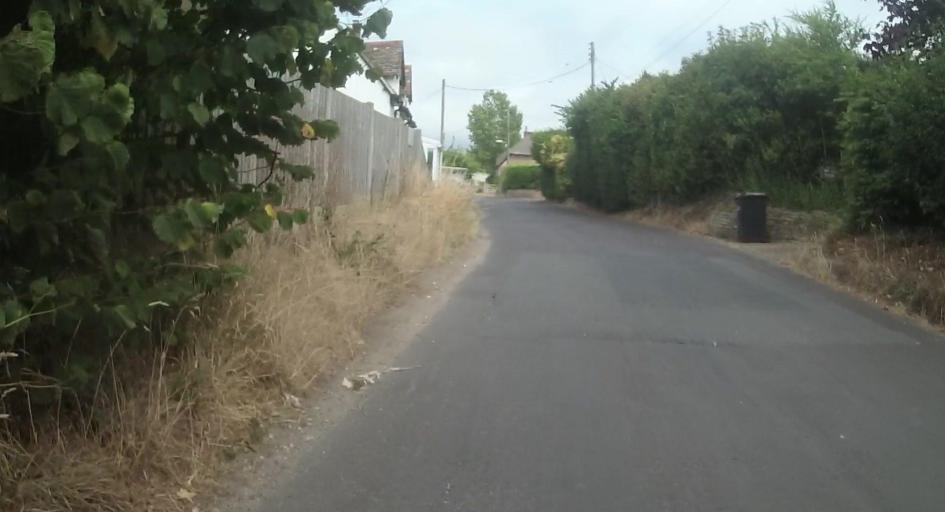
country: GB
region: England
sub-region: Dorset
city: Bovington Camp
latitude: 50.6821
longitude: -2.2394
